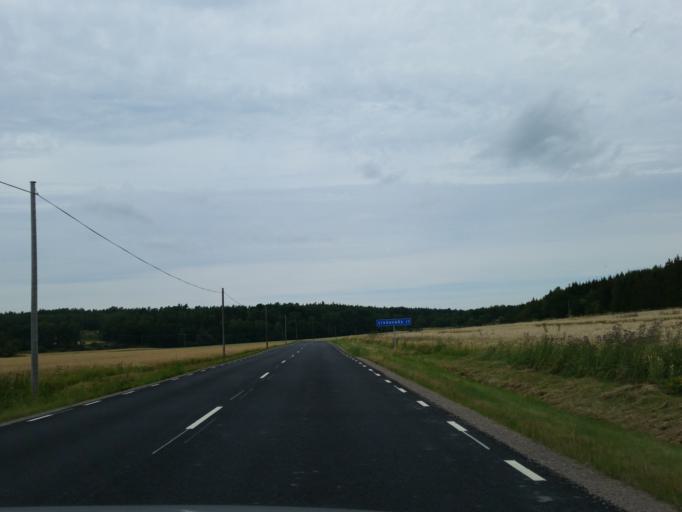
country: SE
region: Soedermanland
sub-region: Strangnas Kommun
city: Mariefred
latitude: 59.2560
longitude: 17.1782
